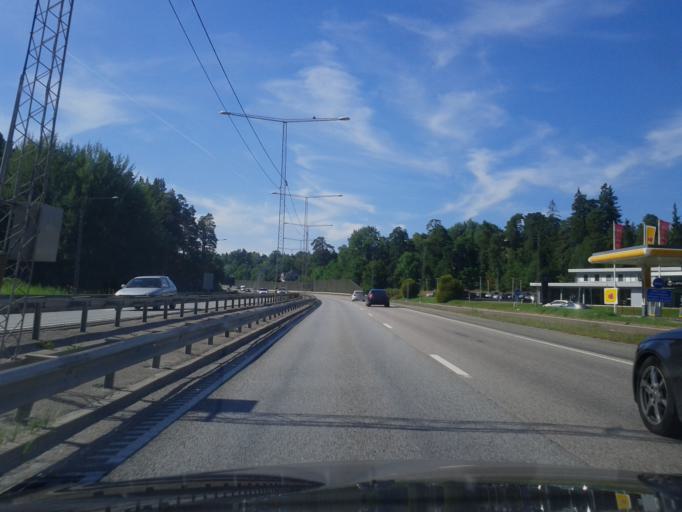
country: SE
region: Stockholm
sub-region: Taby Kommun
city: Taby
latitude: 59.4342
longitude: 18.0686
